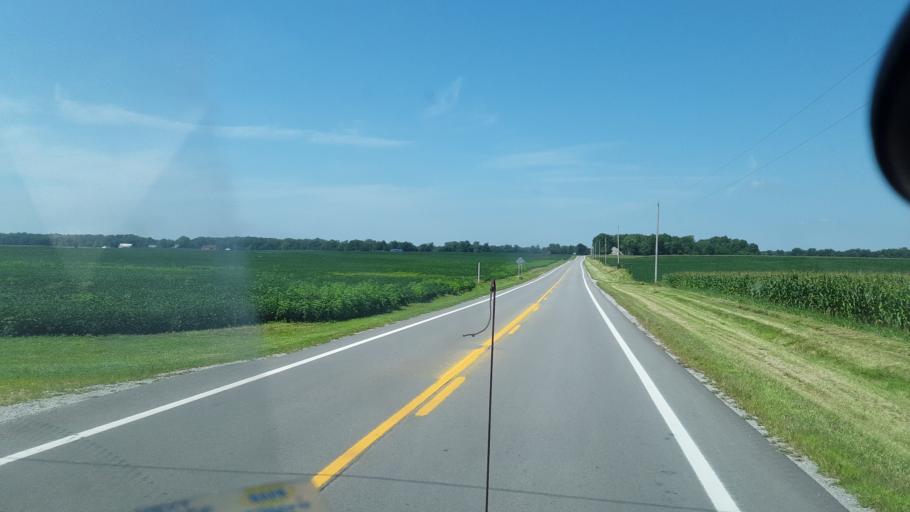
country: US
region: Ohio
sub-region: Wyandot County
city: Carey
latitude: 40.9419
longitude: -83.2842
